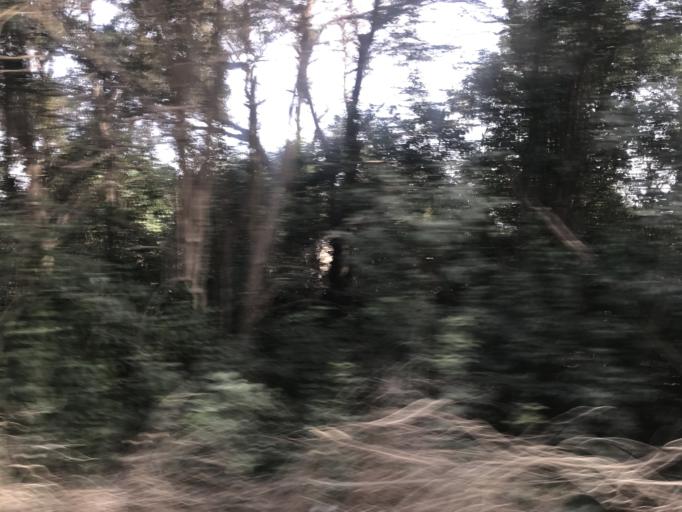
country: AR
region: Cordoba
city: Laguna Larga
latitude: -31.8048
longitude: -63.7787
